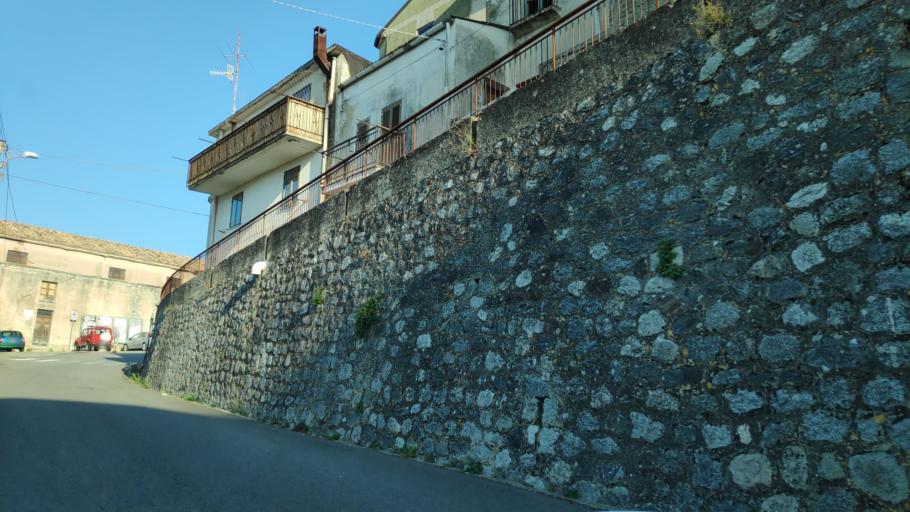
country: IT
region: Calabria
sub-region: Provincia di Catanzaro
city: Satriano
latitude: 38.6697
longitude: 16.4837
